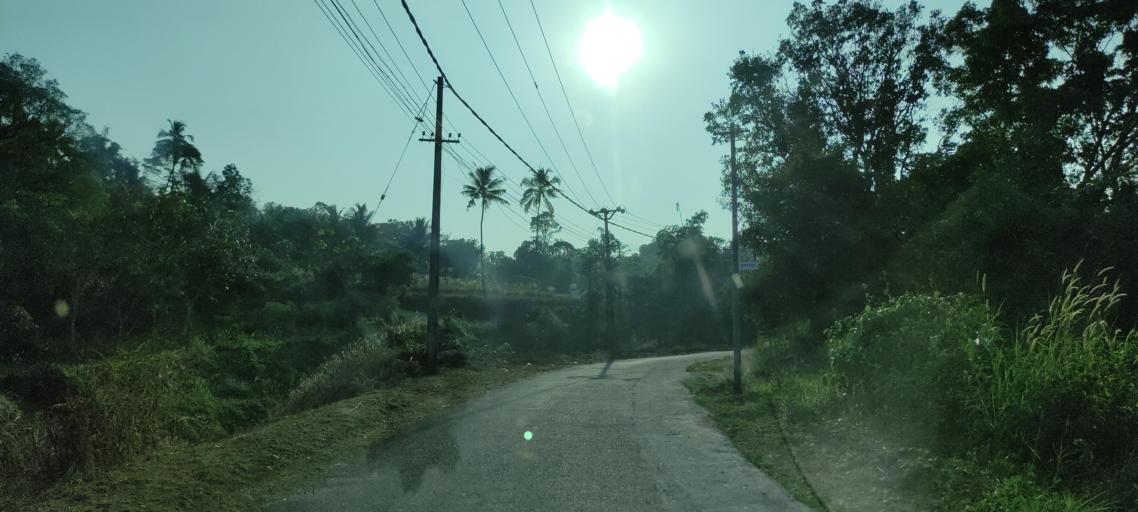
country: IN
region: Kerala
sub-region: Pattanamtitta
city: Adur
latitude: 9.1437
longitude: 76.7393
